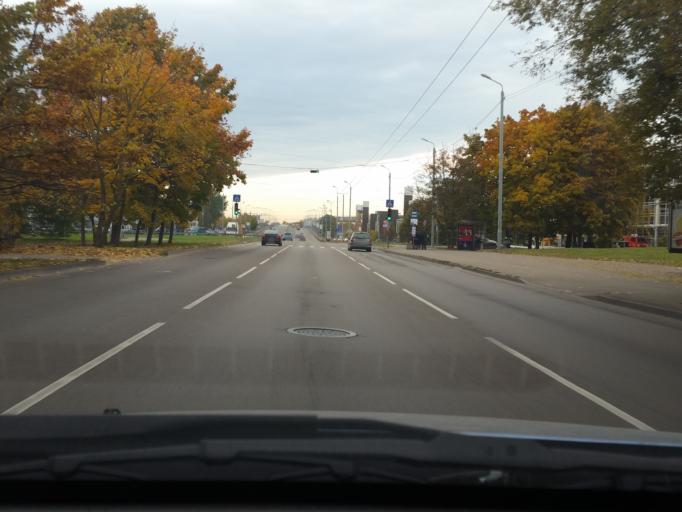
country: LV
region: Riga
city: Riga
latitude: 56.9655
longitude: 24.1678
